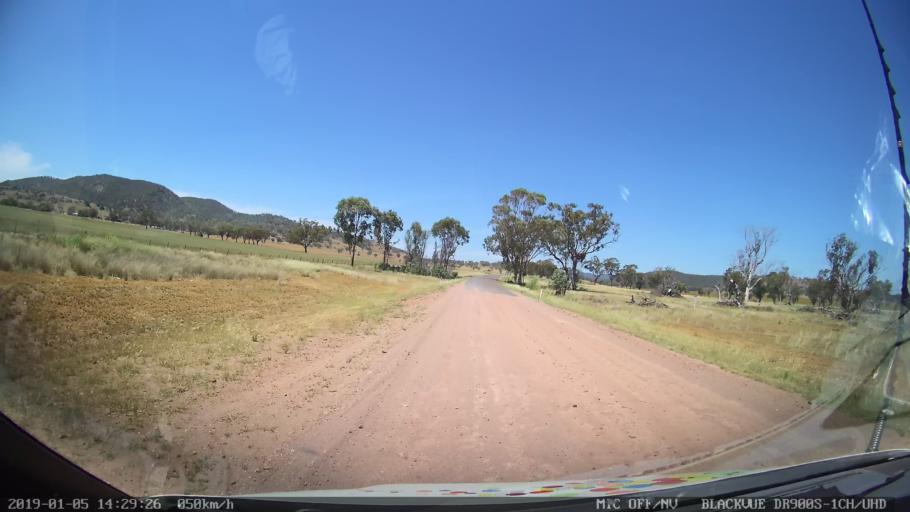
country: AU
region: New South Wales
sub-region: Tamworth Municipality
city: Phillip
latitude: -31.2290
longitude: 150.5816
